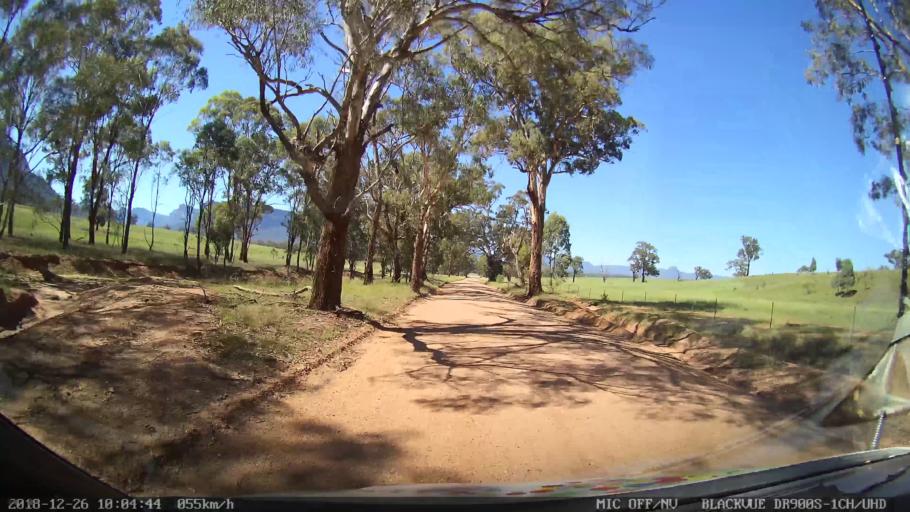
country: AU
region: New South Wales
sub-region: Mid-Western Regional
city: Kandos
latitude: -33.0727
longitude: 150.2131
